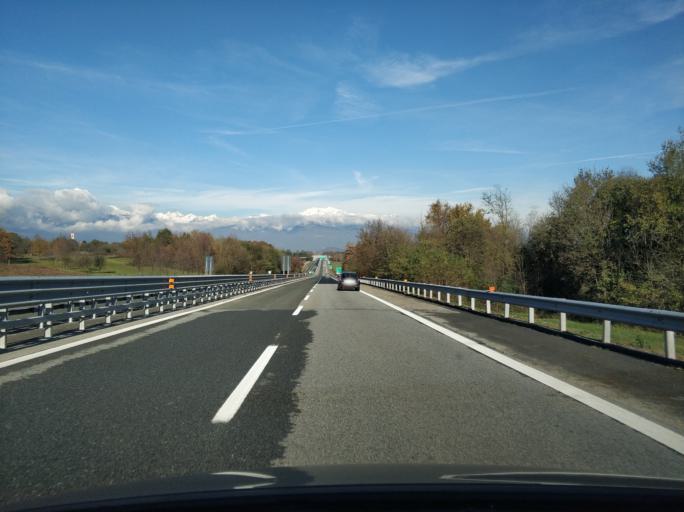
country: IT
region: Piedmont
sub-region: Provincia di Torino
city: Scarmagno
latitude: 45.3766
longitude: 7.8449
